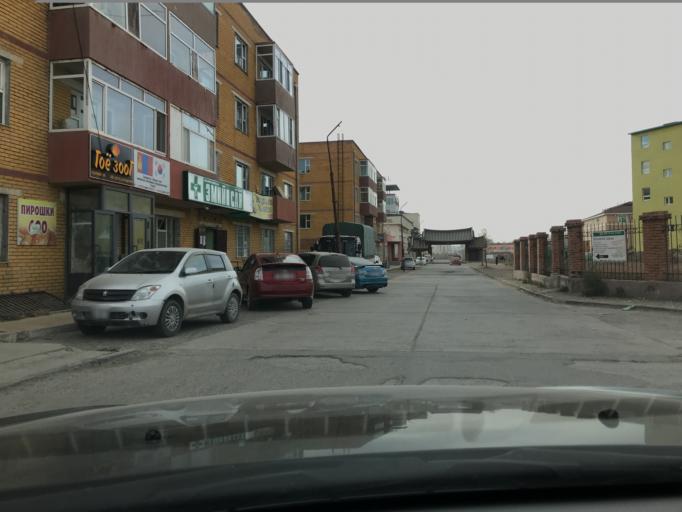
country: MN
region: Ulaanbaatar
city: Ulaanbaatar
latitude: 47.9133
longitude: 106.9759
